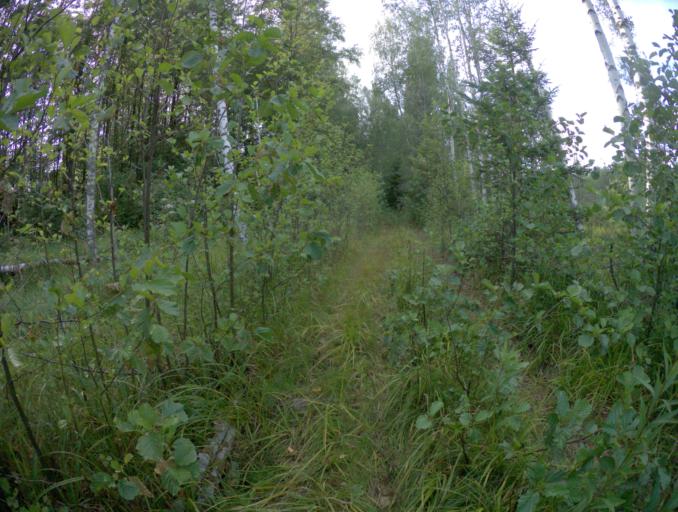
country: RU
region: Vladimir
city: Vorsha
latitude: 55.8990
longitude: 40.1604
